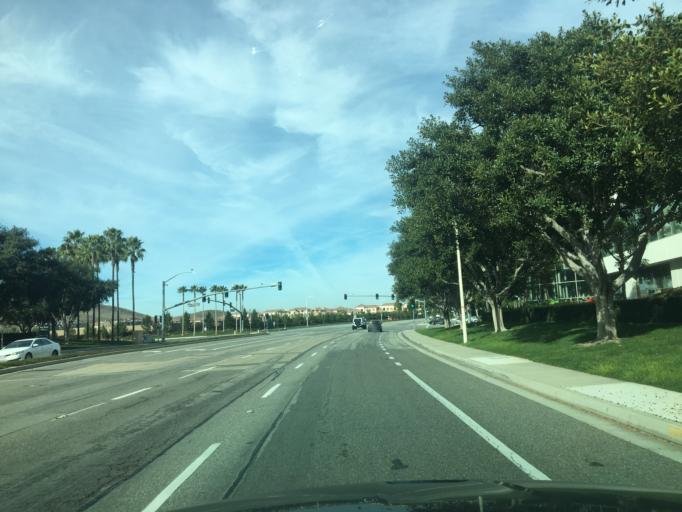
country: US
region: California
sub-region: Orange County
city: Laguna Woods
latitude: 33.6369
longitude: -117.7396
